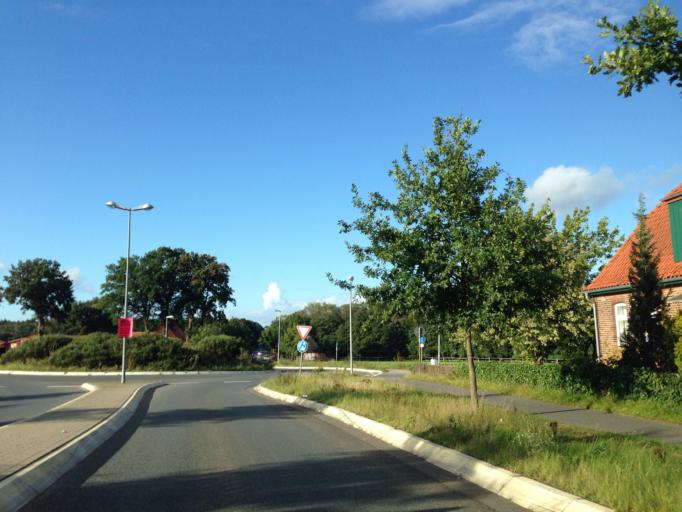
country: DE
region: Lower Saxony
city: Melbeck
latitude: 53.2072
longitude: 10.4054
